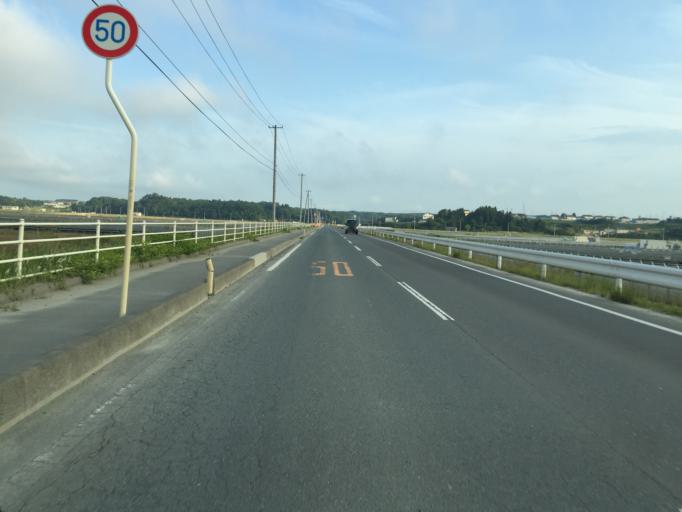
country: JP
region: Miyagi
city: Marumori
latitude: 37.7733
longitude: 140.9811
